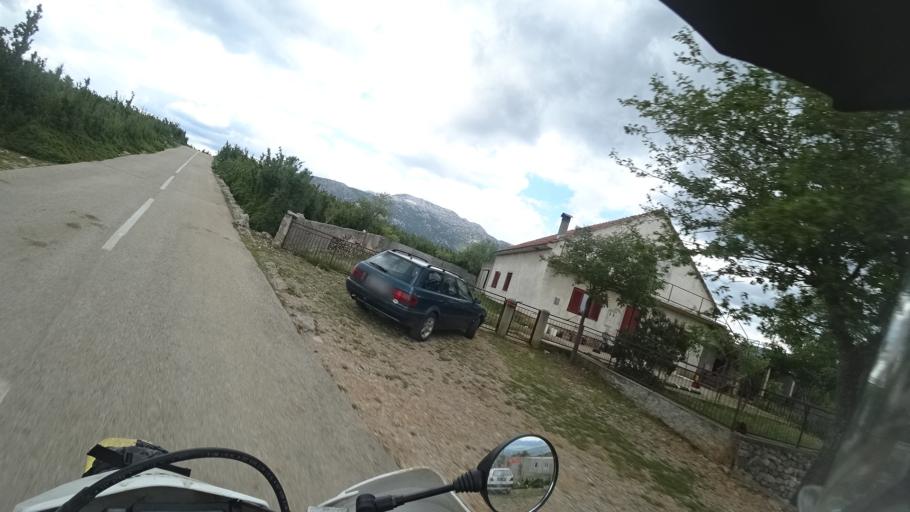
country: HR
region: Zadarska
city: Gracac
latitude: 44.2036
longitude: 15.8577
